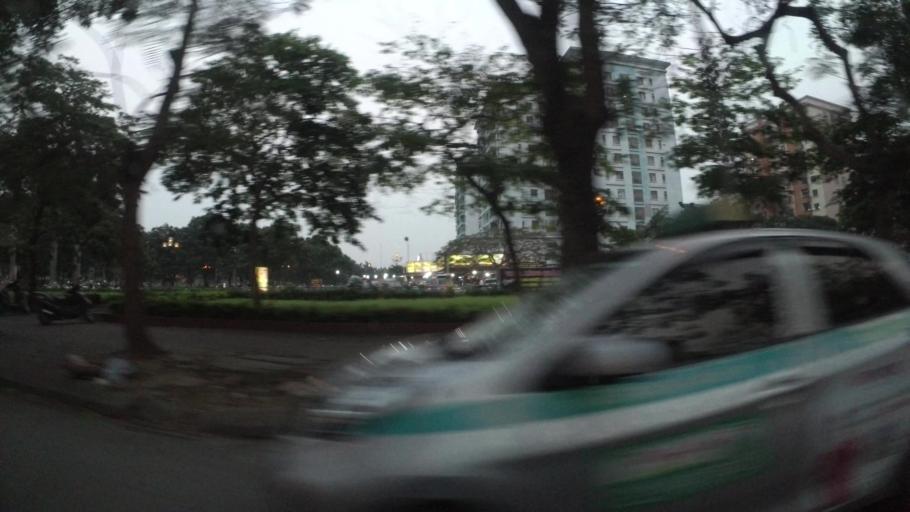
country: VN
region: Ha Noi
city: Ha Dong
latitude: 20.9752
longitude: 105.7887
